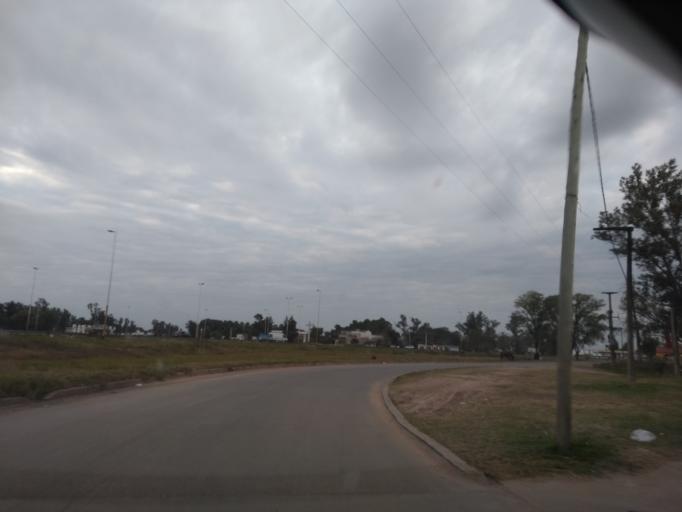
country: AR
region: Chaco
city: Presidencia Roque Saenz Pena
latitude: -26.8142
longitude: -60.4188
